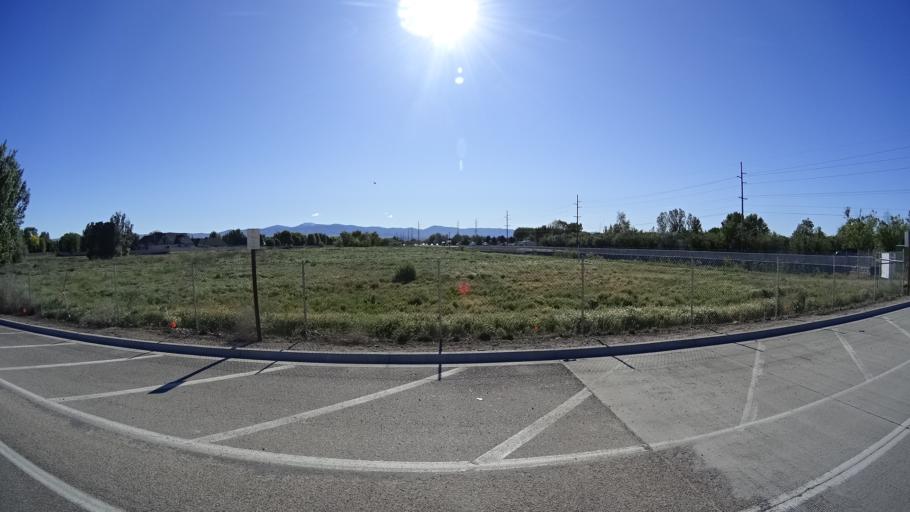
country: US
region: Idaho
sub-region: Ada County
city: Eagle
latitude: 43.6947
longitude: -116.4137
